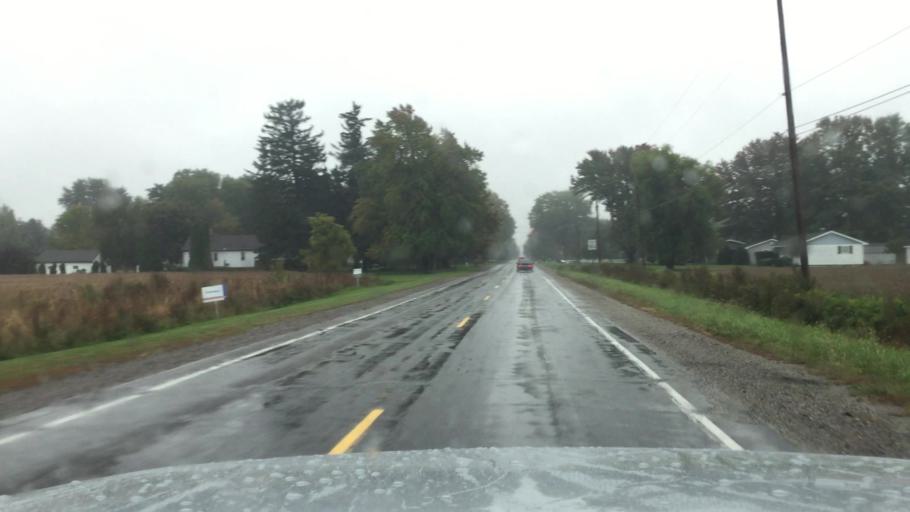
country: US
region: Michigan
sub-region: Saginaw County
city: Bridgeport
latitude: 43.3509
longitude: -83.9346
